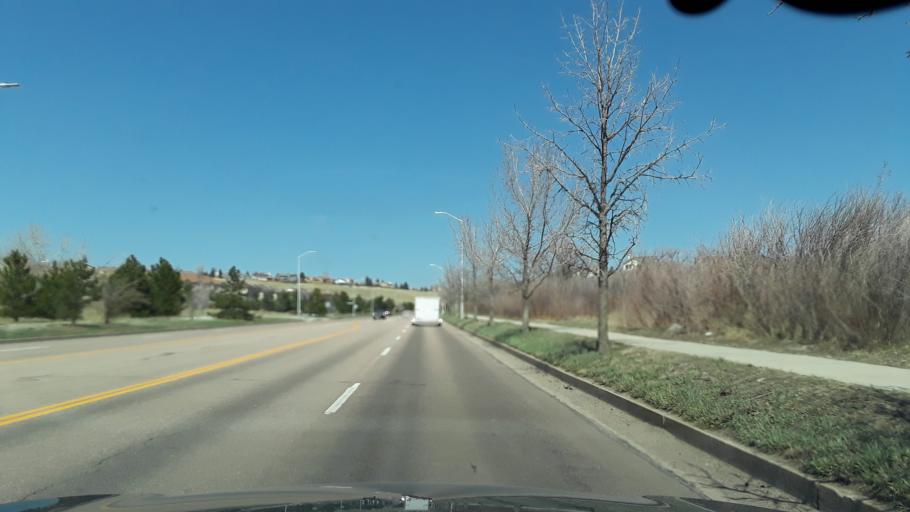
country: US
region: Colorado
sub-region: El Paso County
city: Black Forest
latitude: 38.9441
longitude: -104.7420
